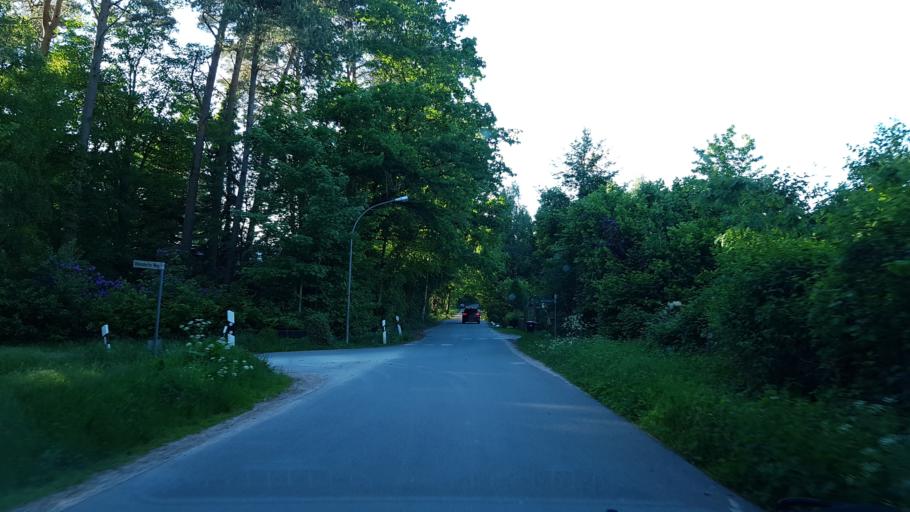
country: DE
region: Lower Saxony
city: Stelle
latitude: 53.3557
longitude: 10.1049
